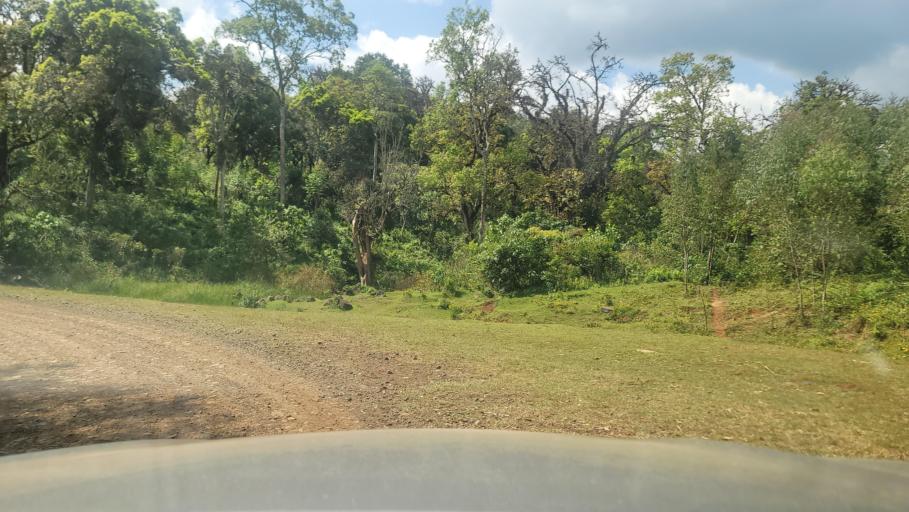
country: ET
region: Southern Nations, Nationalities, and People's Region
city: Bonga
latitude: 7.6965
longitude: 36.2445
